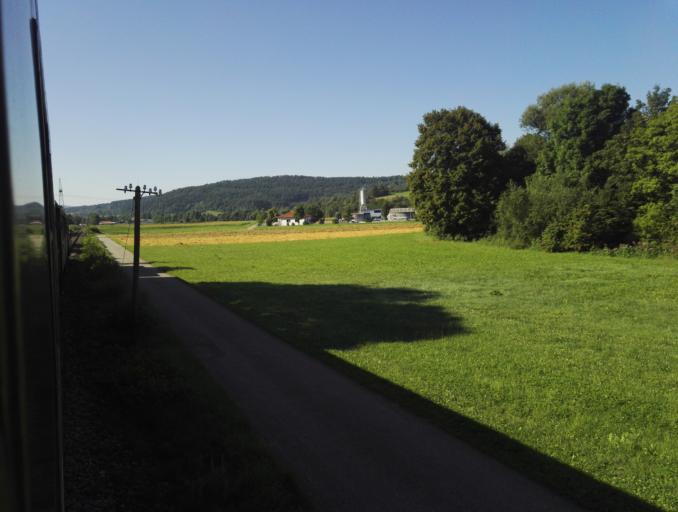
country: DE
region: Baden-Wuerttemberg
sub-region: Regierungsbezirk Stuttgart
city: Rudersberg
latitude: 48.8548
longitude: 9.5381
